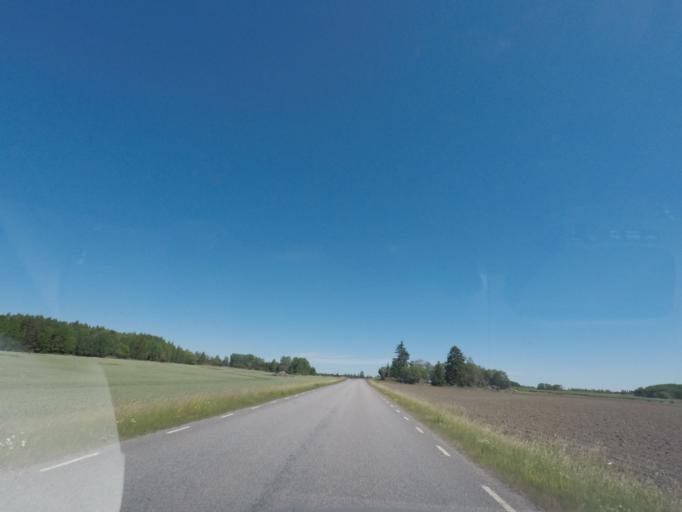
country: SE
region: Uppsala
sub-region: Enkopings Kommun
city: Irsta
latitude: 59.6773
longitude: 16.9455
